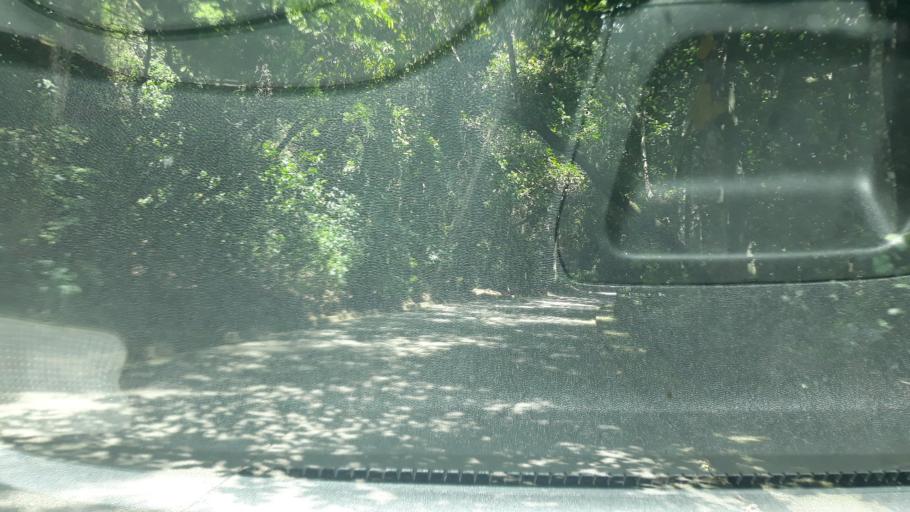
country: BR
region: Rio de Janeiro
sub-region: Rio De Janeiro
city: Rio de Janeiro
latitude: -22.9483
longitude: -43.2084
